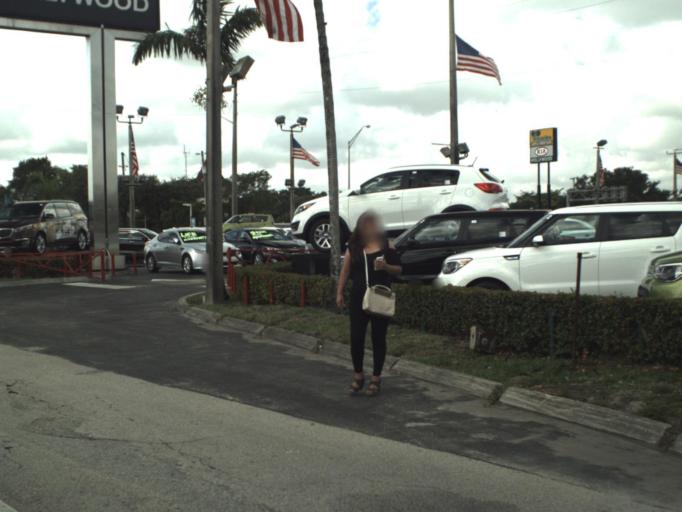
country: US
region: Florida
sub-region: Broward County
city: West Park
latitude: 25.9959
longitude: -80.2072
